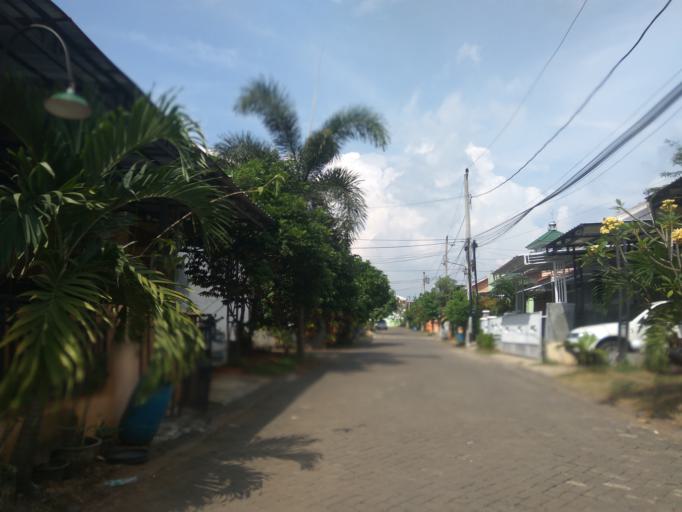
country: ID
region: Central Java
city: Ungaran
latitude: -7.0729
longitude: 110.4442
